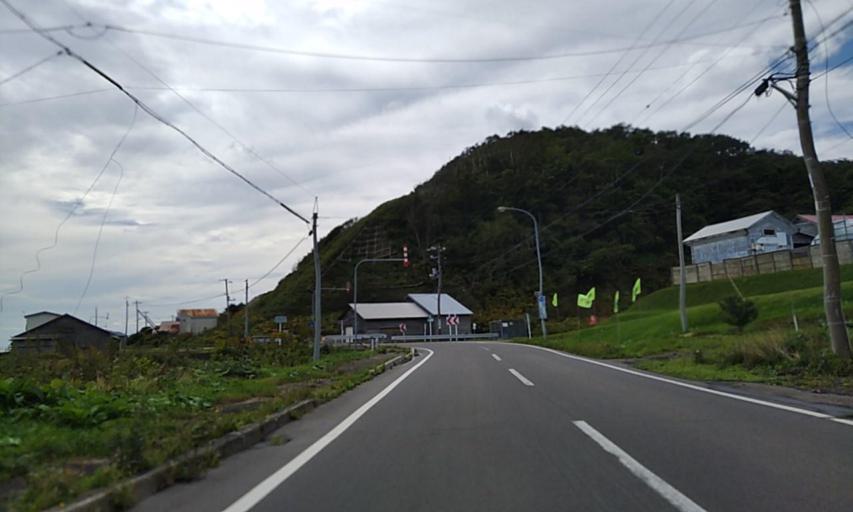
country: JP
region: Hokkaido
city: Kushiro
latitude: 42.7992
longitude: 143.8098
